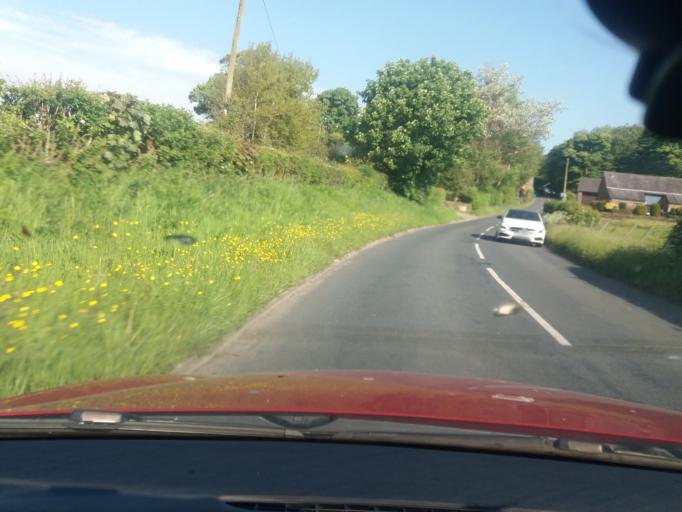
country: GB
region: England
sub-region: Borough of Wigan
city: Haigh
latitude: 53.6145
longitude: -2.5784
